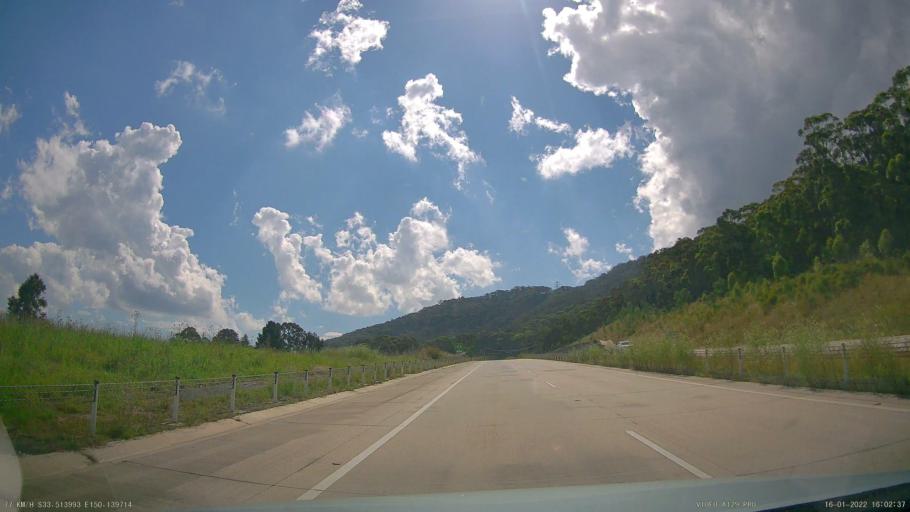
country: AU
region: New South Wales
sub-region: Lithgow
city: Bowenfels
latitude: -33.5140
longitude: 150.1392
